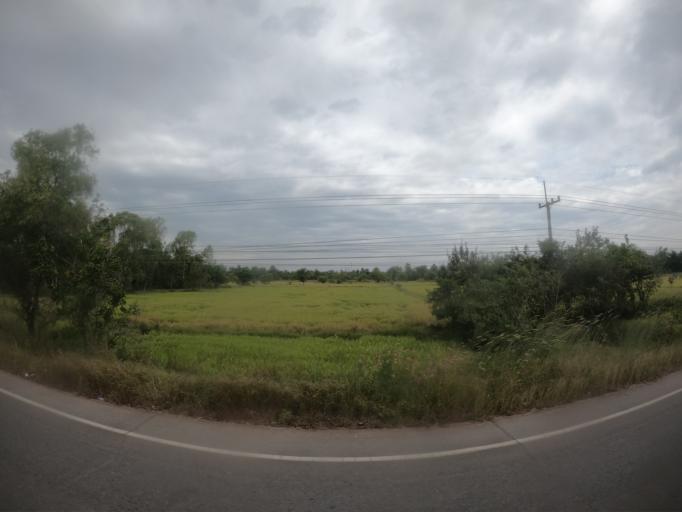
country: TH
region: Maha Sarakham
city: Kantharawichai
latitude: 16.3332
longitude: 103.2369
